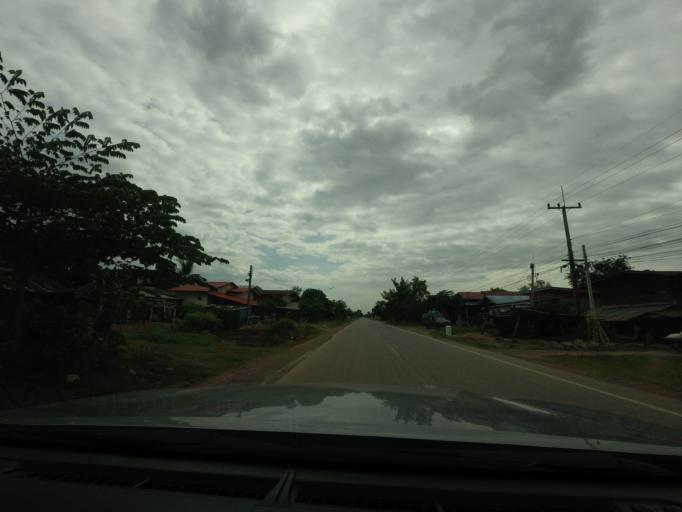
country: TH
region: Phitsanulok
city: Noen Maprang
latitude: 16.6376
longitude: 100.6174
